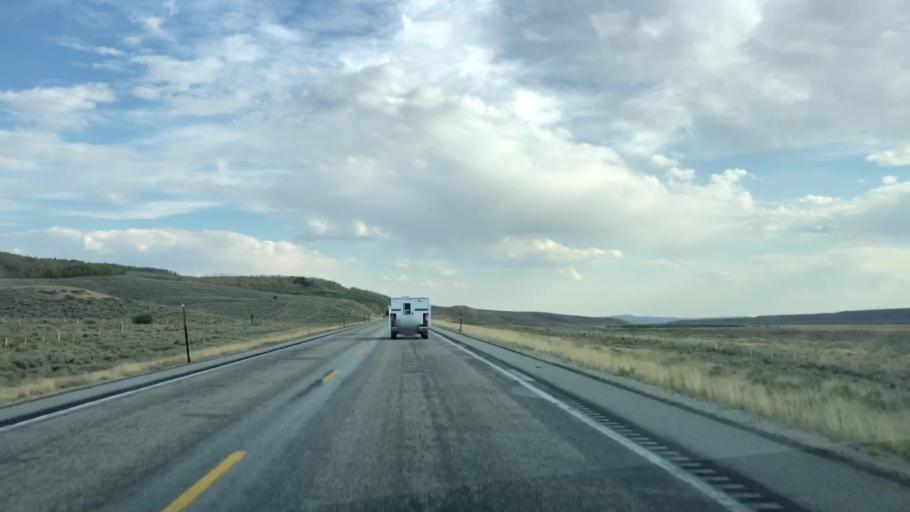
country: US
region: Wyoming
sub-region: Sublette County
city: Pinedale
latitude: 43.0966
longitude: -110.1674
